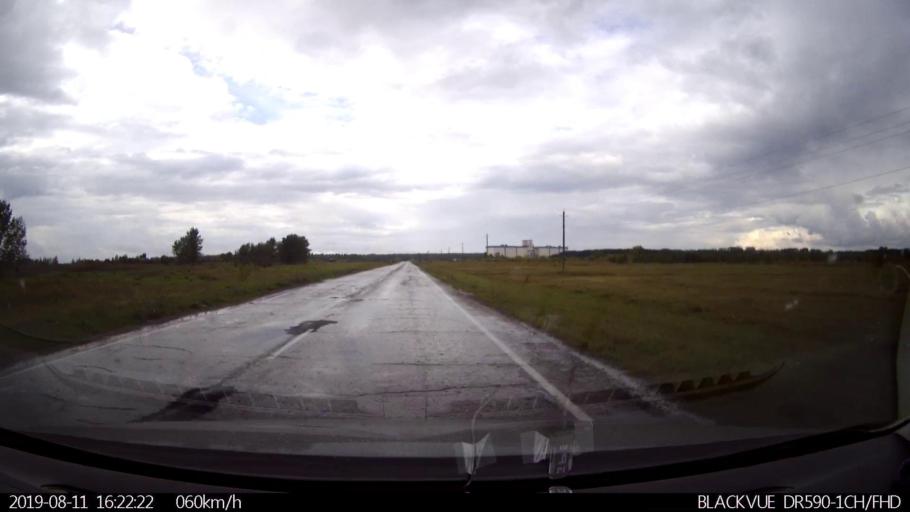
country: RU
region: Ulyanovsk
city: Mayna
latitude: 54.0874
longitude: 47.5933
